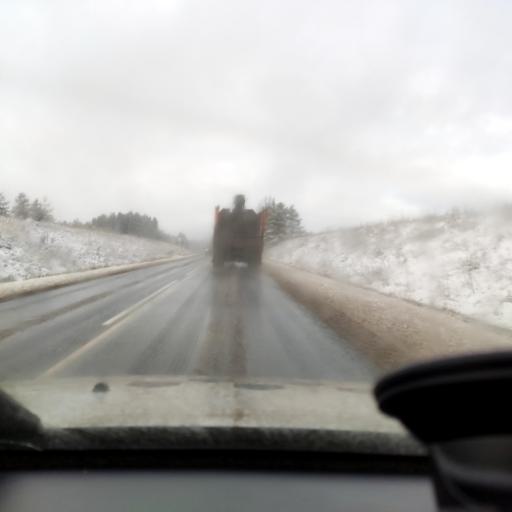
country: RU
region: Perm
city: Nytva
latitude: 57.9672
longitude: 55.3640
